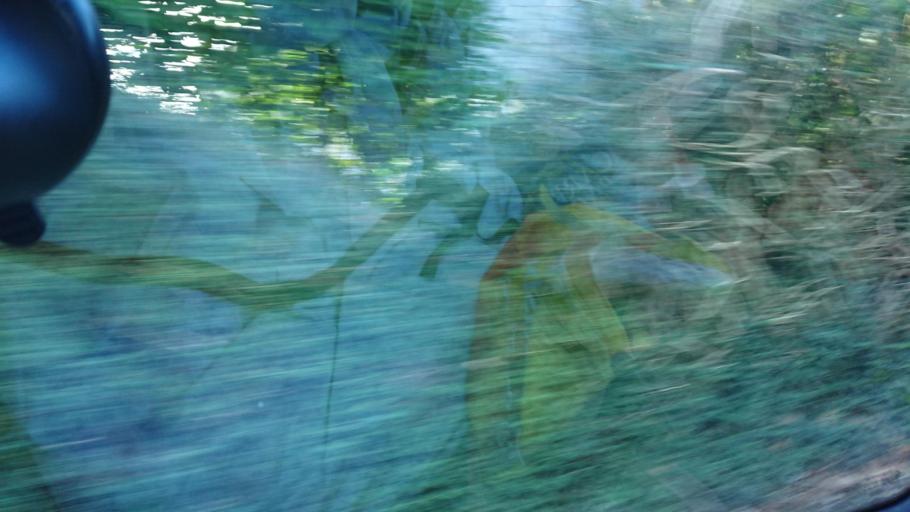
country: GB
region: England
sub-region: Devon
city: Ivybridge
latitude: 50.3614
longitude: -3.9146
